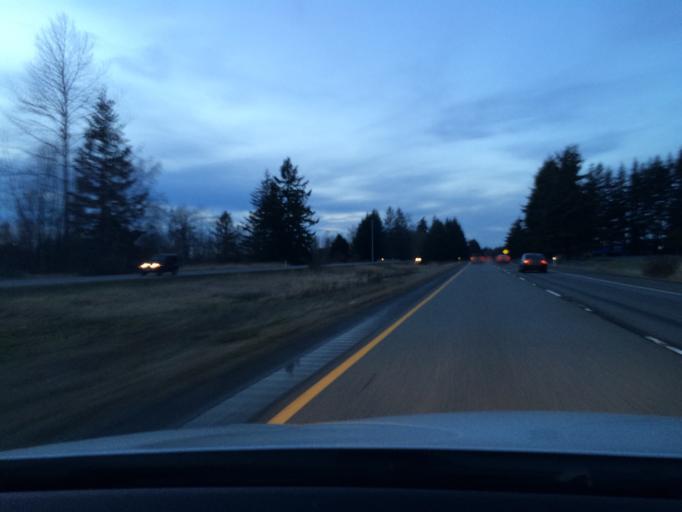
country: US
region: Washington
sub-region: Whatcom County
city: Ferndale
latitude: 48.9079
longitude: -122.6218
